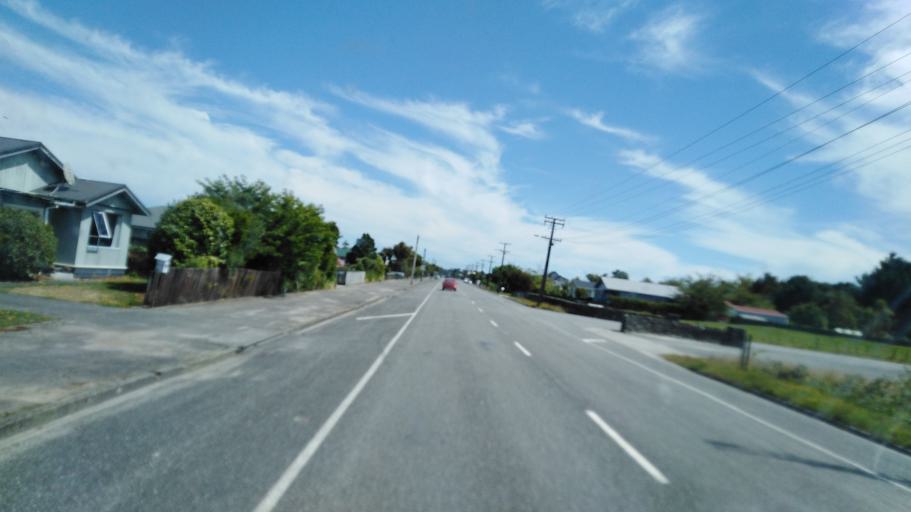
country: NZ
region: West Coast
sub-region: Buller District
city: Westport
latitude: -41.7533
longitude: 171.6155
